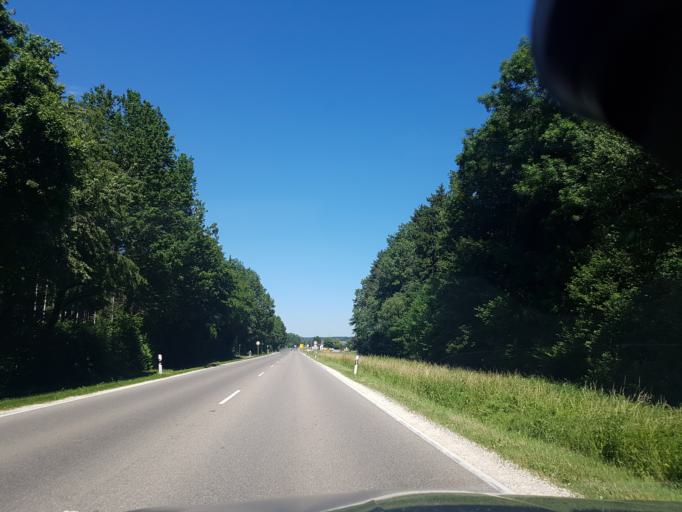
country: DE
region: Bavaria
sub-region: Swabia
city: Weissenhorn
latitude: 48.2911
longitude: 10.1336
